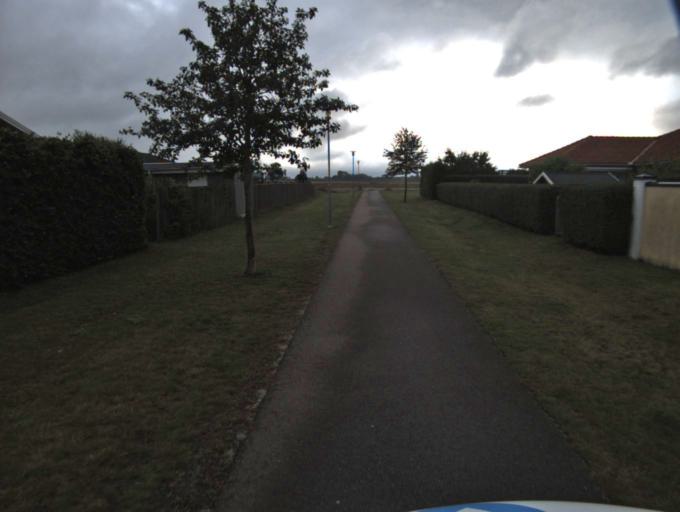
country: SE
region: Skane
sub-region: Kavlinge Kommun
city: Loddekopinge
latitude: 55.7645
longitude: 13.0278
